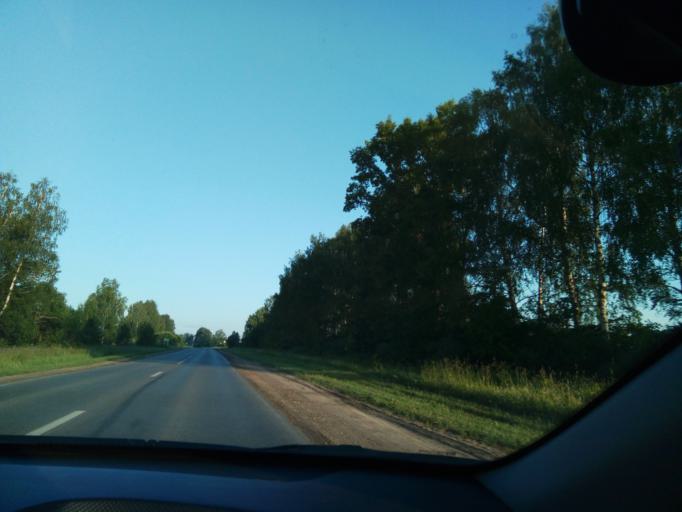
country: RU
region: Nizjnij Novgorod
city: Satis
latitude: 54.9384
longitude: 43.2533
